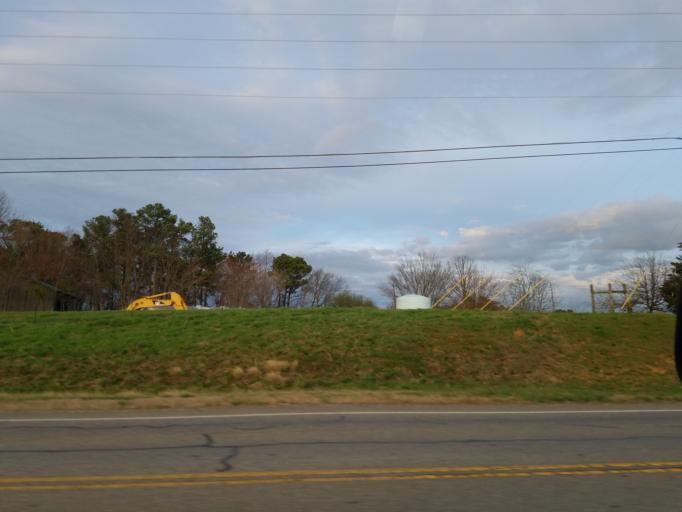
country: US
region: Georgia
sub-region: Pickens County
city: Jasper
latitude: 34.4760
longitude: -84.5271
